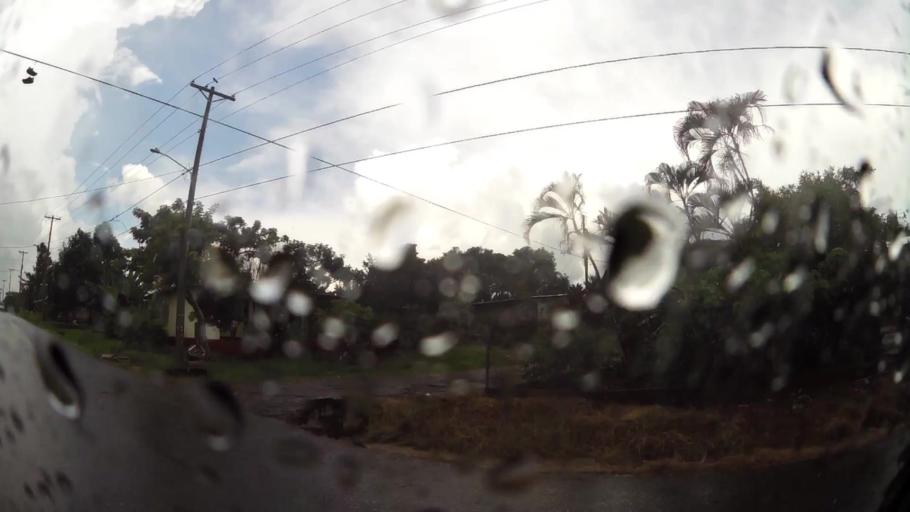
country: PA
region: Panama
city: Cabra Numero Uno
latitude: 9.1081
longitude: -79.3381
